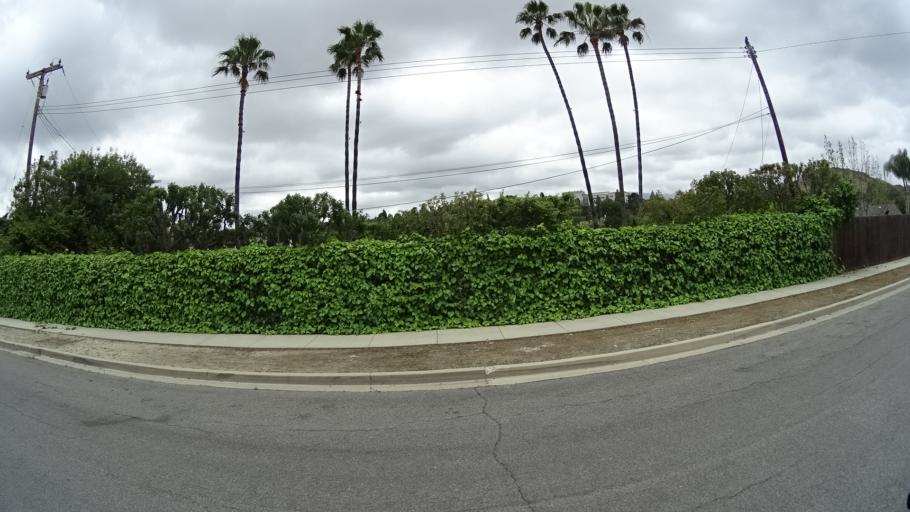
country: US
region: California
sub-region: Ventura County
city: Thousand Oaks
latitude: 34.2118
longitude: -118.8812
